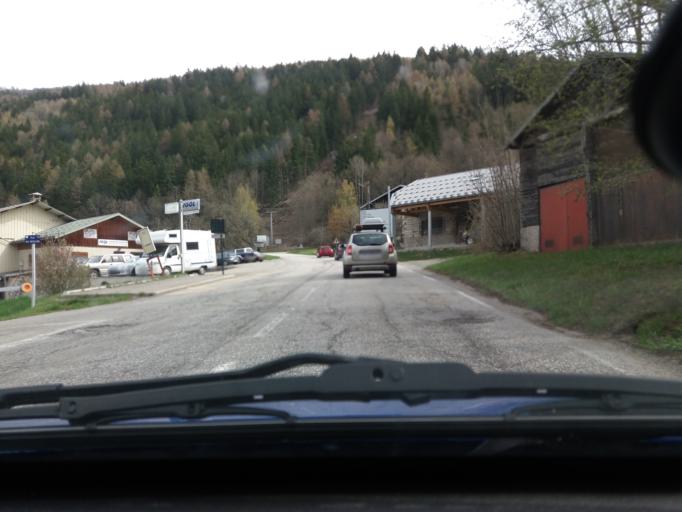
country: FR
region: Rhone-Alpes
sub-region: Departement de la Savoie
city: Macot-la-Plagne
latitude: 45.5511
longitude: 6.6624
